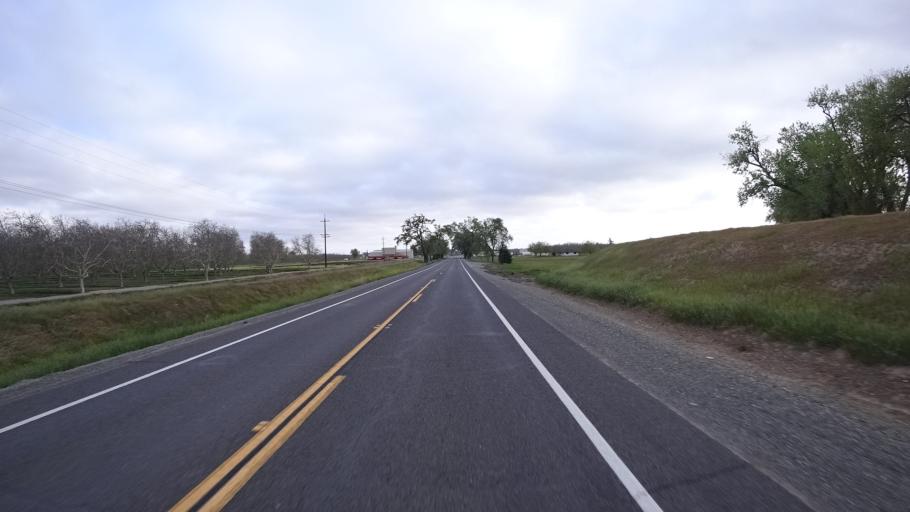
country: US
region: California
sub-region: Glenn County
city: Willows
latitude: 39.4524
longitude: -122.0174
